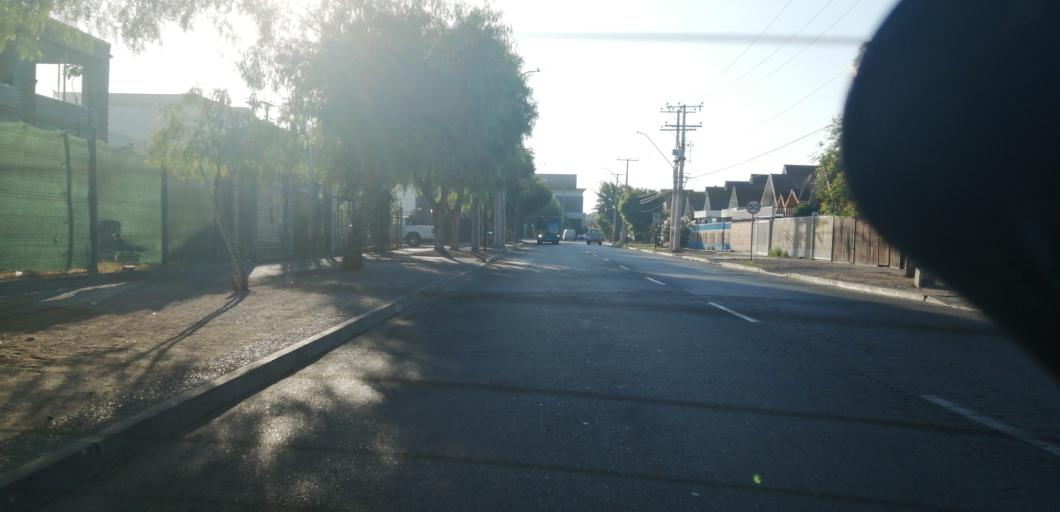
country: CL
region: Santiago Metropolitan
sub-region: Provincia de Santiago
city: Lo Prado
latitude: -33.4334
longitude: -70.7764
